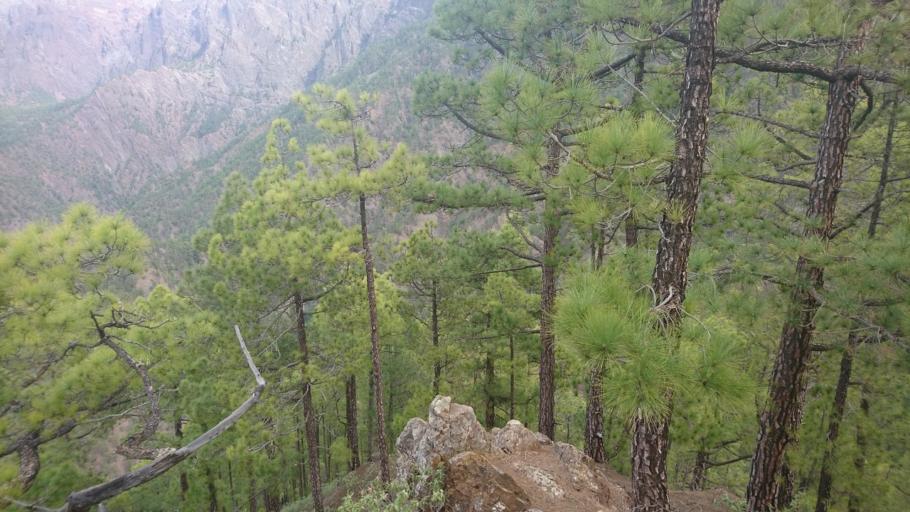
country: ES
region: Canary Islands
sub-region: Provincia de Santa Cruz de Tenerife
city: El Paso
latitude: 28.7005
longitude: -17.8641
